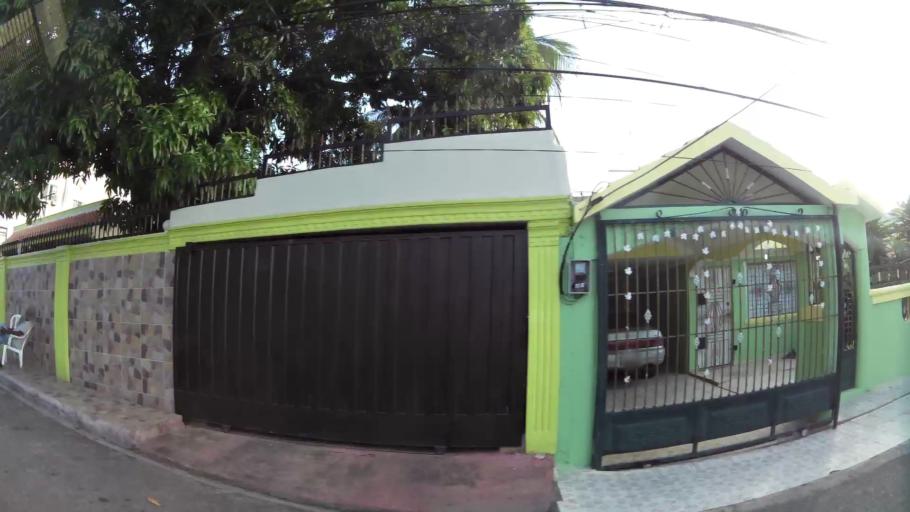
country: DO
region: Nacional
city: Ensanche Luperon
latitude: 18.5451
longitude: -69.9058
